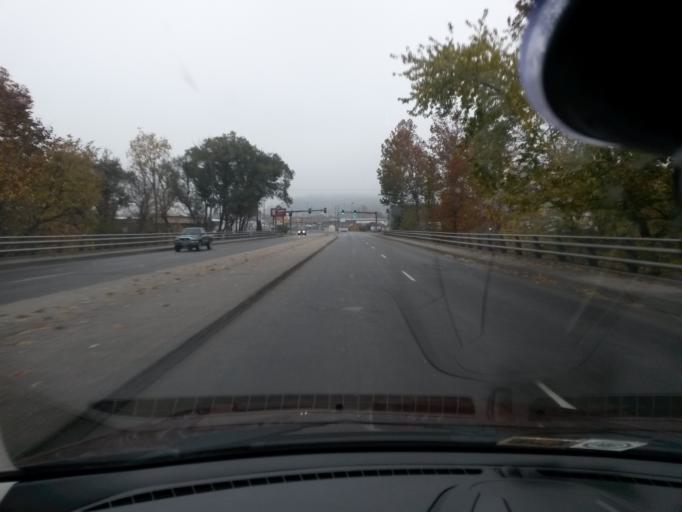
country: US
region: Virginia
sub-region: City of Covington
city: Fairlawn
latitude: 37.7780
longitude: -79.9911
